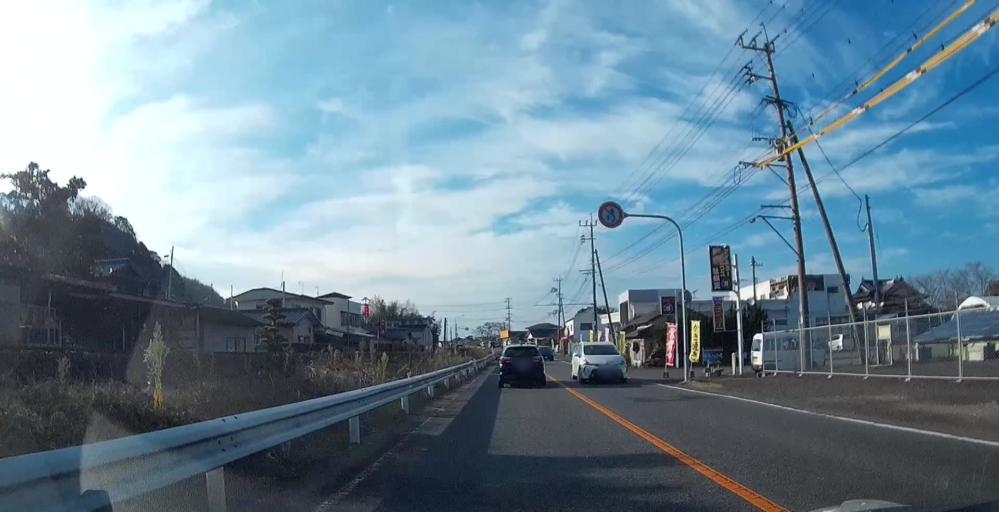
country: JP
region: Kumamoto
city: Uto
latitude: 32.7040
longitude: 130.5917
